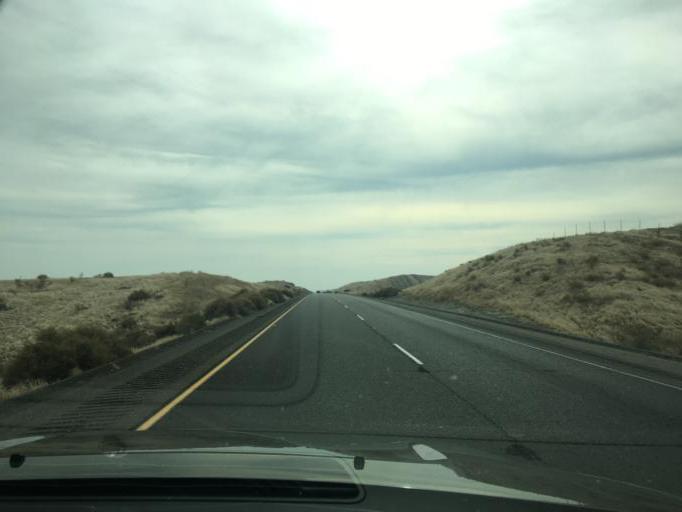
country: US
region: California
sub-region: Fresno County
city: Mendota
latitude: 36.4878
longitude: -120.4425
